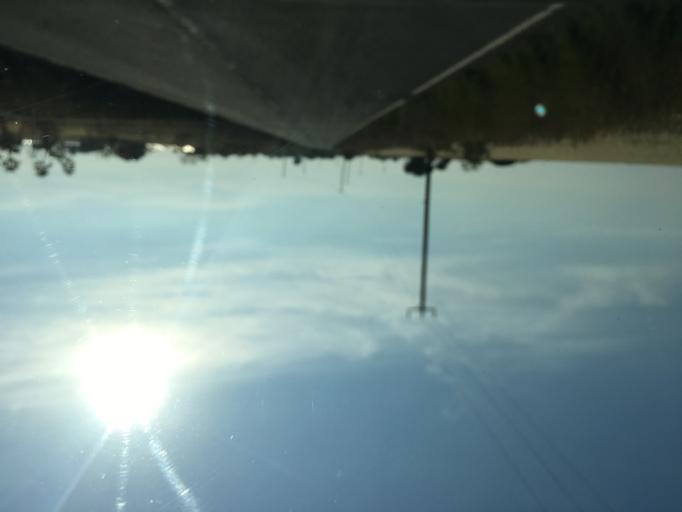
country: CY
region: Larnaka
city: Kofinou
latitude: 34.7465
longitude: 33.3910
